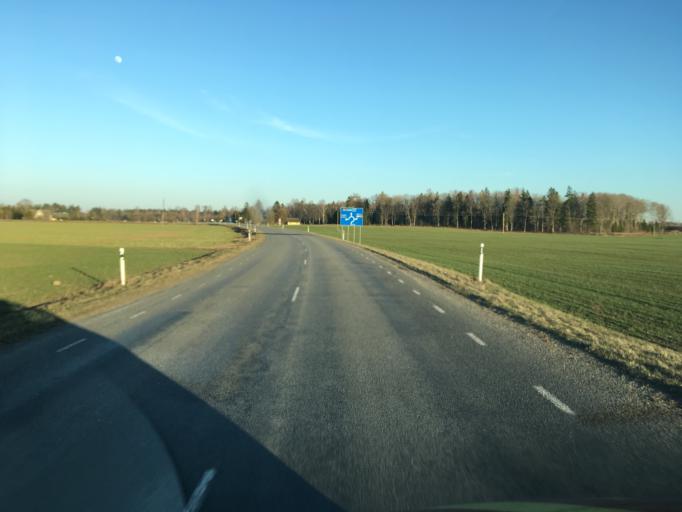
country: EE
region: Raplamaa
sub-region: Kehtna vald
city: Kehtna
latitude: 59.0573
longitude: 24.9443
